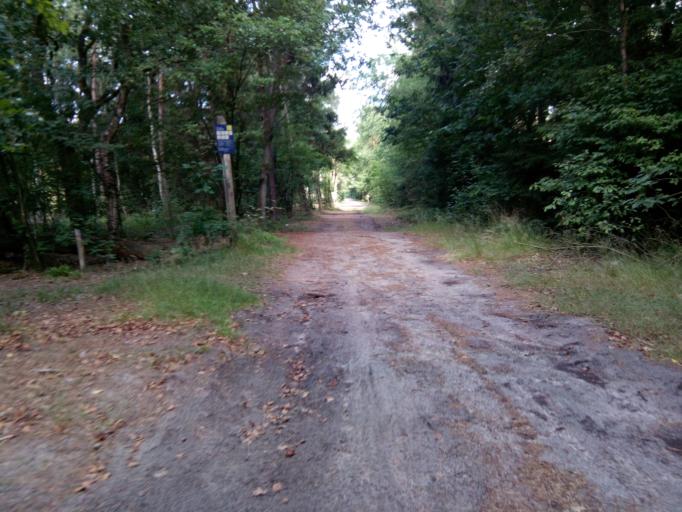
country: NL
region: Utrecht
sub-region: Gemeente Utrechtse Heuvelrug
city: Maarn
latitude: 52.0758
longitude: 5.3637
